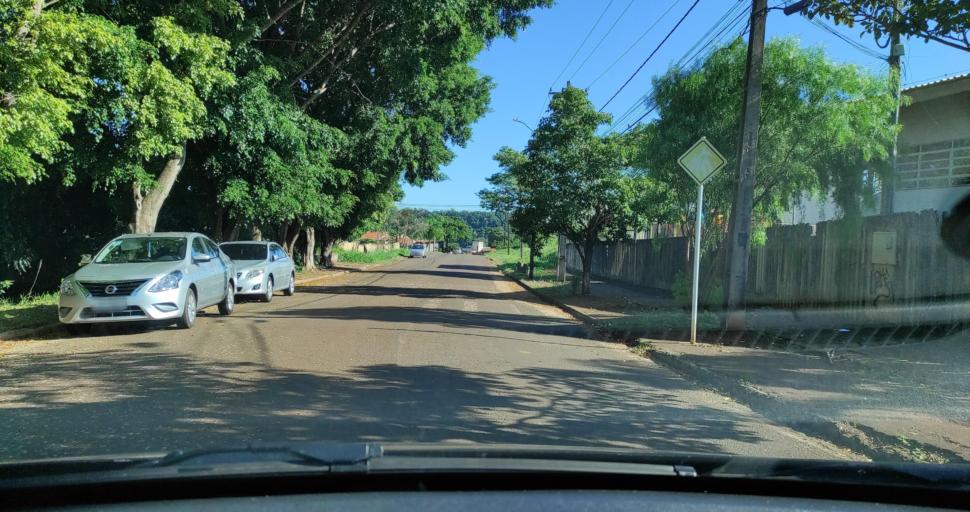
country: BR
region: Parana
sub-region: Ibipora
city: Ibipora
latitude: -23.2606
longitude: -51.0618
